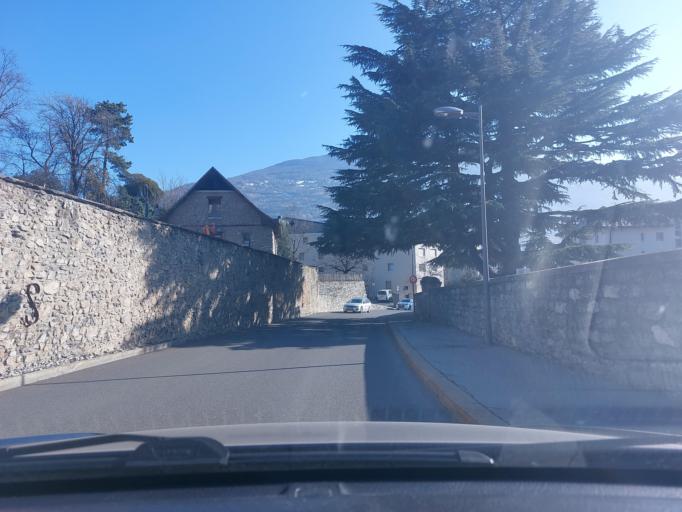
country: CH
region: Valais
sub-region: Sion District
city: Sitten
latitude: 46.2373
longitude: 7.3585
